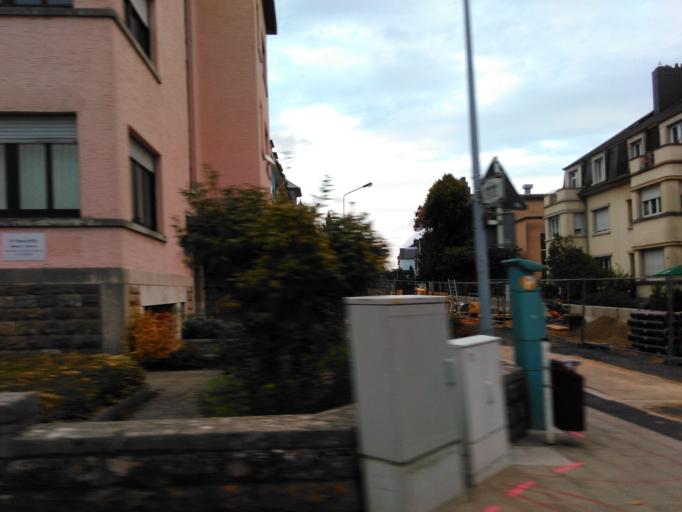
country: LU
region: Luxembourg
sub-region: Canton de Luxembourg
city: Luxembourg
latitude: 49.6218
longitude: 6.1209
